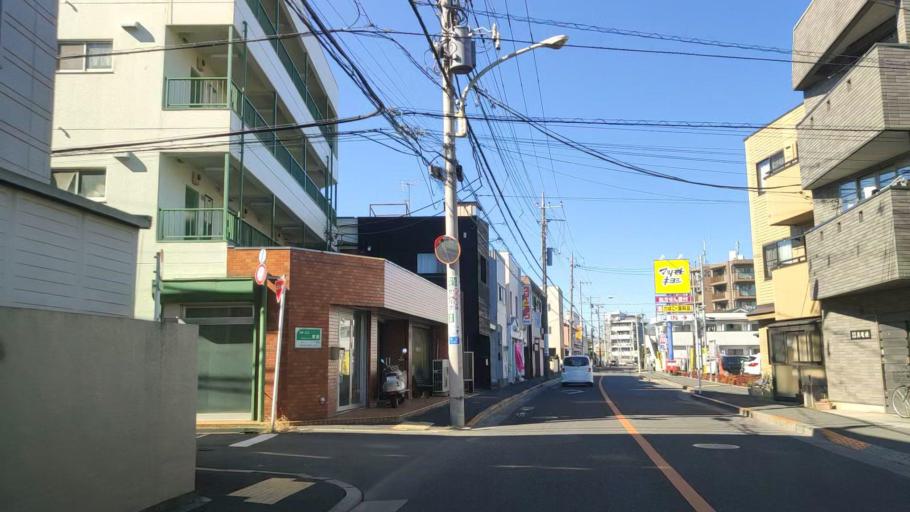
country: JP
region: Tokyo
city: Mitaka-shi
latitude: 35.6664
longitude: 139.5780
